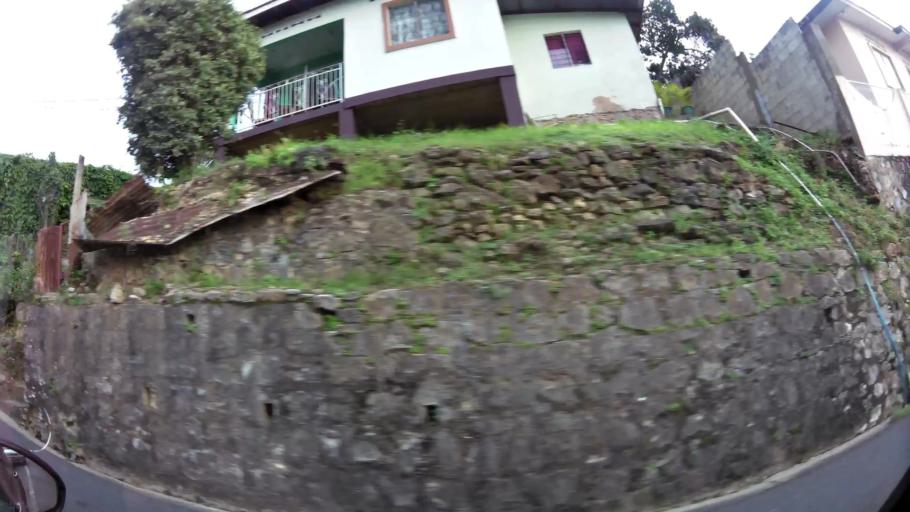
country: TT
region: San Juan/Laventille
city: Laventille
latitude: 10.6568
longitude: -61.4977
